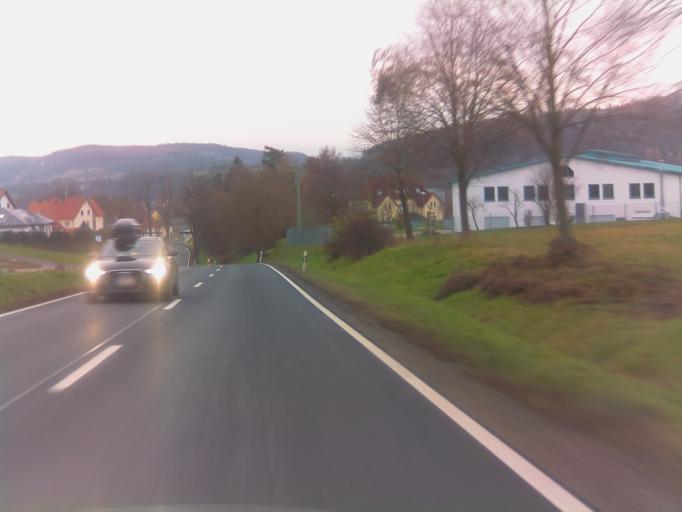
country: DE
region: Thuringia
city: Buttlar
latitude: 50.7632
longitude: 9.9564
